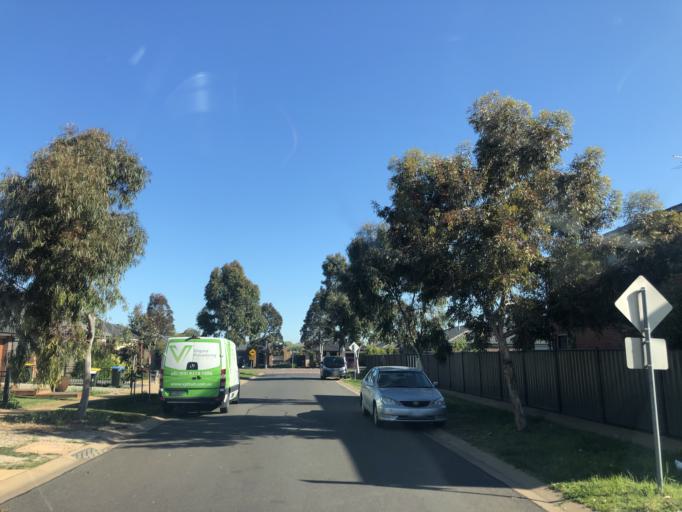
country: AU
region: Victoria
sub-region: Wyndham
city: Hoppers Crossing
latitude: -37.8940
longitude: 144.7192
